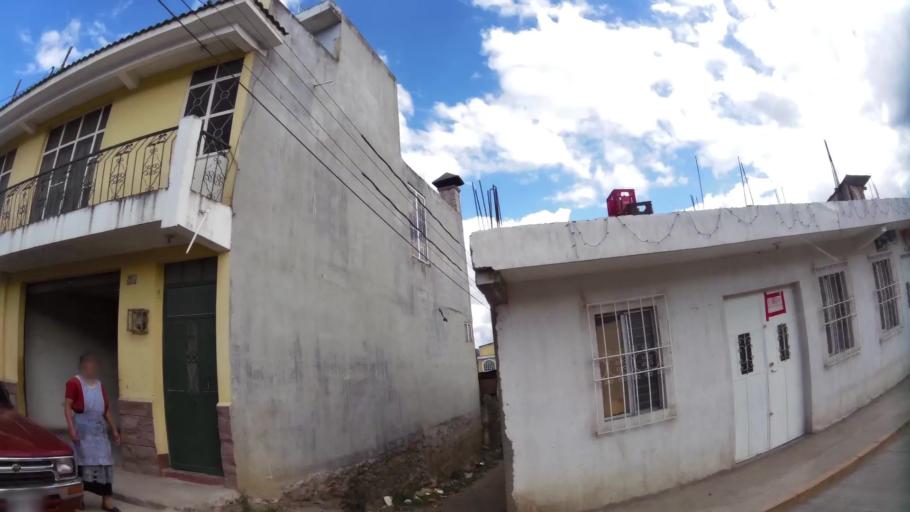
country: GT
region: Quetzaltenango
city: Quetzaltenango
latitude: 14.8348
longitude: -91.5427
